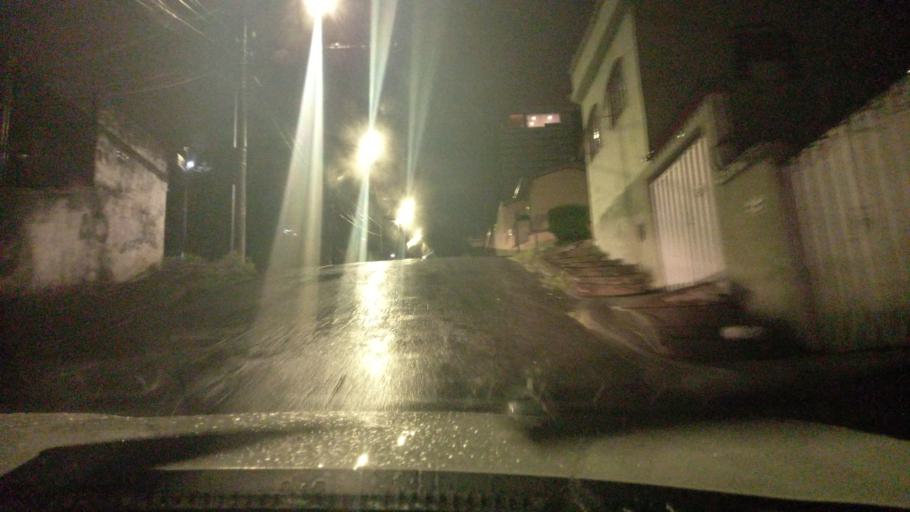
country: BR
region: Minas Gerais
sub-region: Belo Horizonte
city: Belo Horizonte
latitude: -19.8997
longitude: -43.9204
